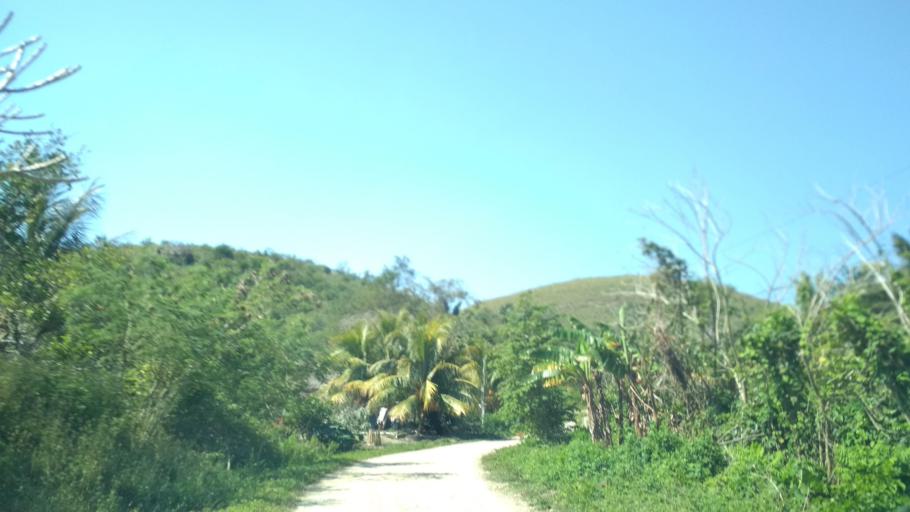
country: MX
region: Veracruz
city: Gutierrez Zamora
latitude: 20.4892
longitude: -97.1628
